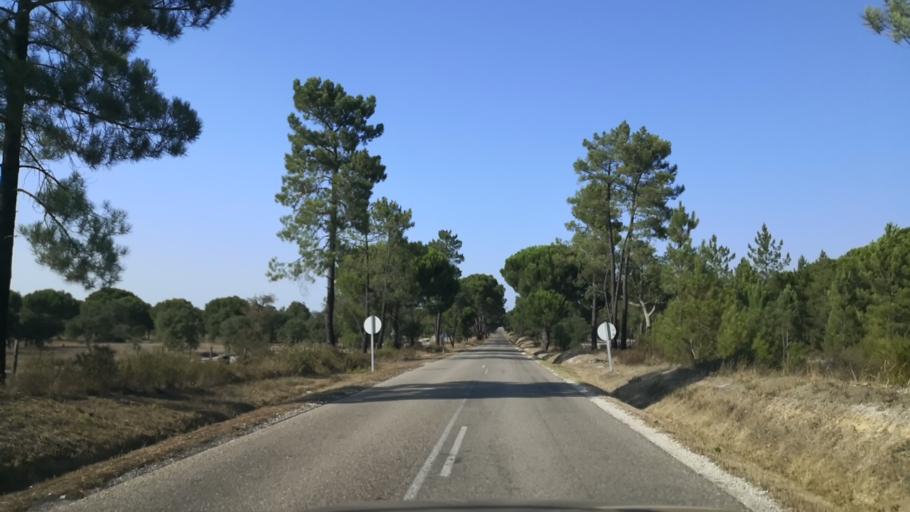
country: PT
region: Santarem
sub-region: Coruche
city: Coruche
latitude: 38.9042
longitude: -8.5277
